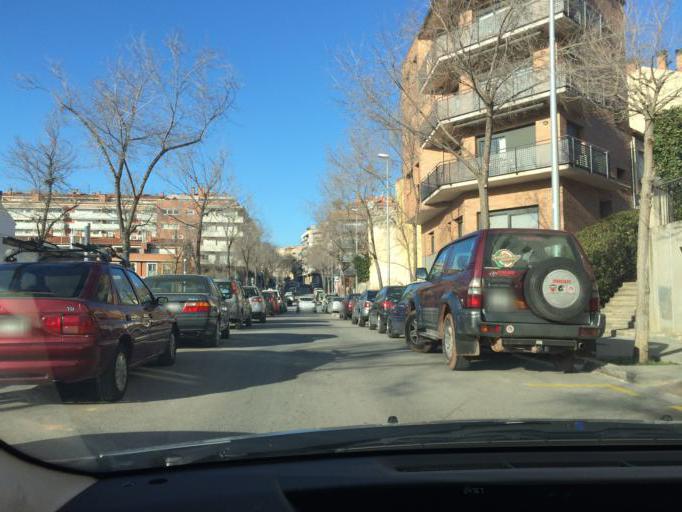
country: ES
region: Catalonia
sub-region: Provincia de Barcelona
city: Manresa
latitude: 41.7349
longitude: 1.8309
